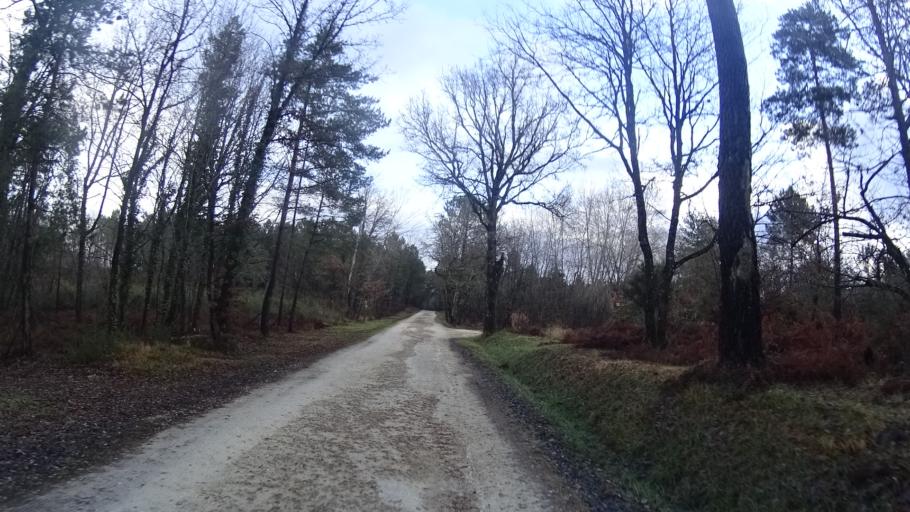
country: FR
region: Aquitaine
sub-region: Departement de la Dordogne
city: Antonne-et-Trigonant
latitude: 45.2055
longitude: 0.8598
